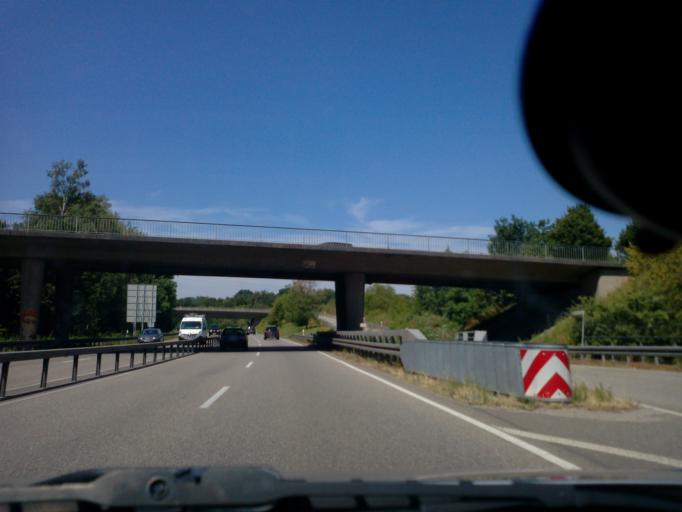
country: DE
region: Baden-Wuerttemberg
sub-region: Freiburg Region
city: Offenburg
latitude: 48.4692
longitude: 7.9237
